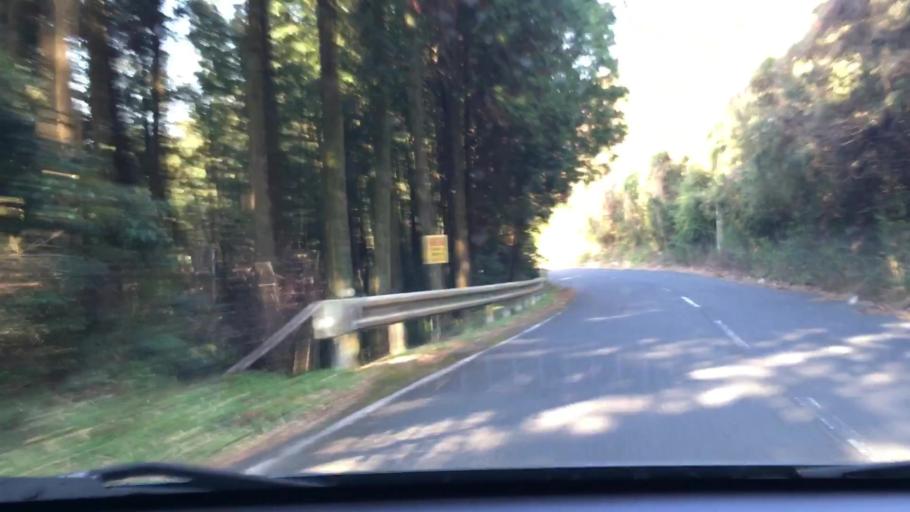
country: JP
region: Kagoshima
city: Kokubu-matsuki
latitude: 31.6662
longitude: 130.8259
